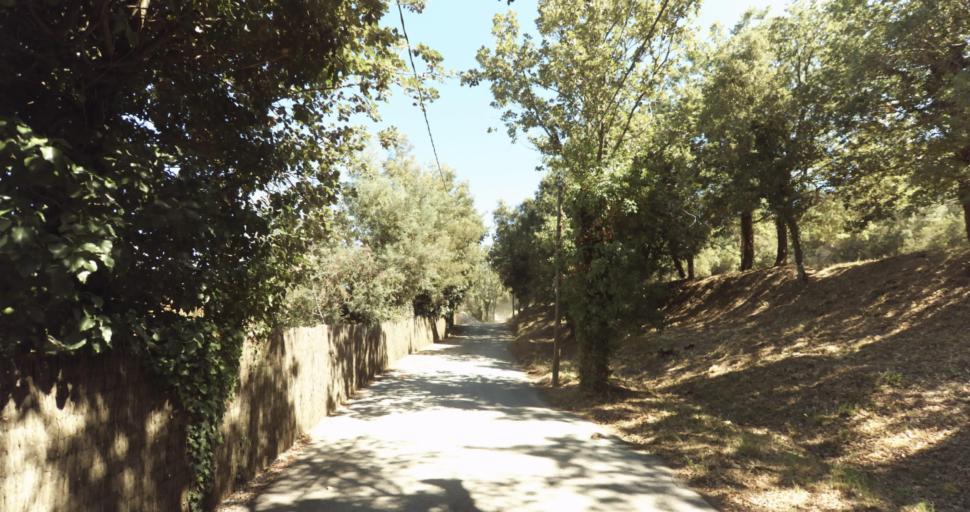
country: FR
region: Provence-Alpes-Cote d'Azur
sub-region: Departement du Var
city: Gassin
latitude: 43.2353
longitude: 6.5789
